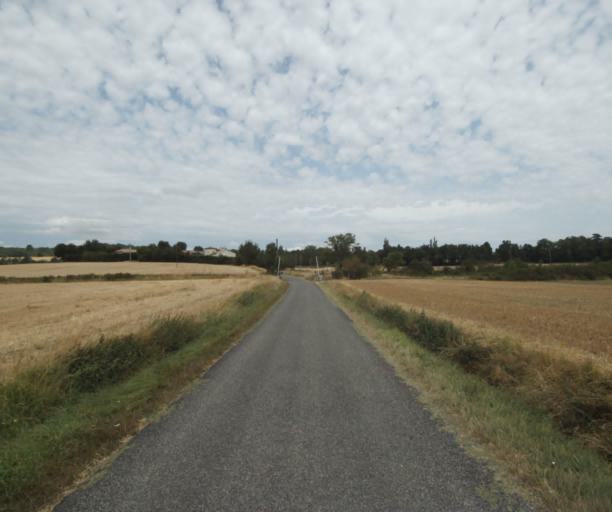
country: FR
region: Midi-Pyrenees
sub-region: Departement de la Haute-Garonne
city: Saint-Felix-Lauragais
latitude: 43.4231
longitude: 1.8999
